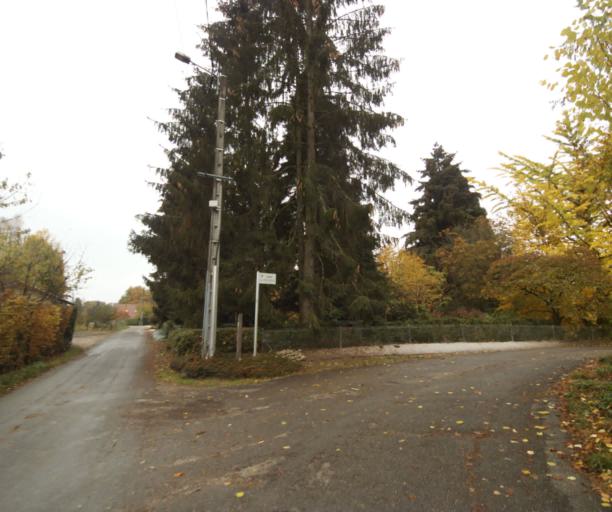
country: FR
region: Rhone-Alpes
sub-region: Departement de la Haute-Savoie
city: Cornier
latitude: 46.1263
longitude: 6.2999
